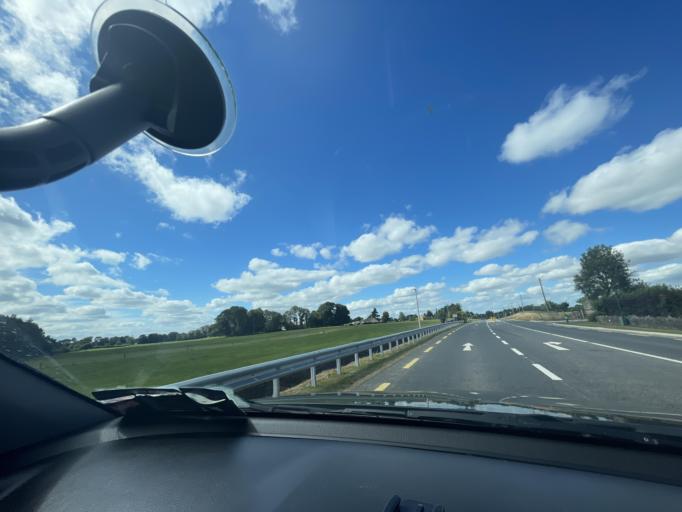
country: IE
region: Leinster
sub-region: An Mhi
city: Newtown Trim
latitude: 53.5247
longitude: -6.6661
